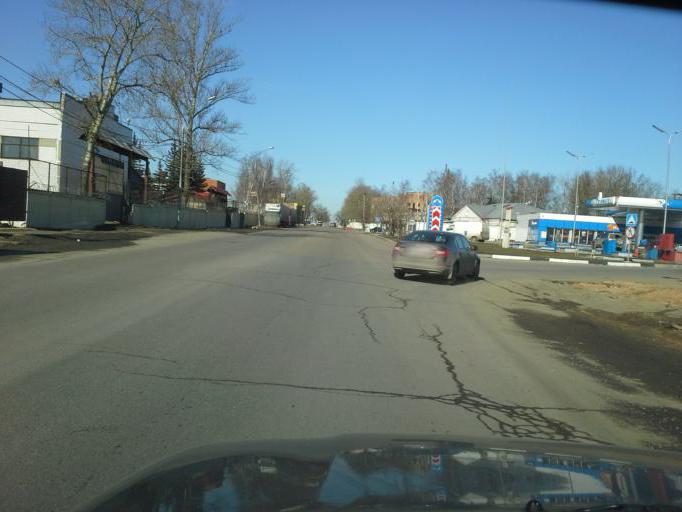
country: RU
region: Moskovskaya
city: Odintsovo
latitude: 55.6510
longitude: 37.2622
